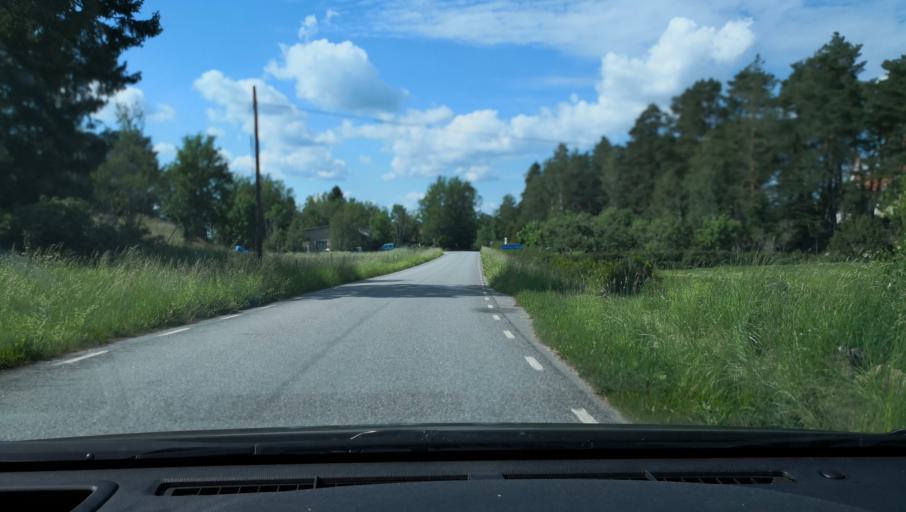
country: SE
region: Uppsala
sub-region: Enkopings Kommun
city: Orsundsbro
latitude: 59.8256
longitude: 17.3196
